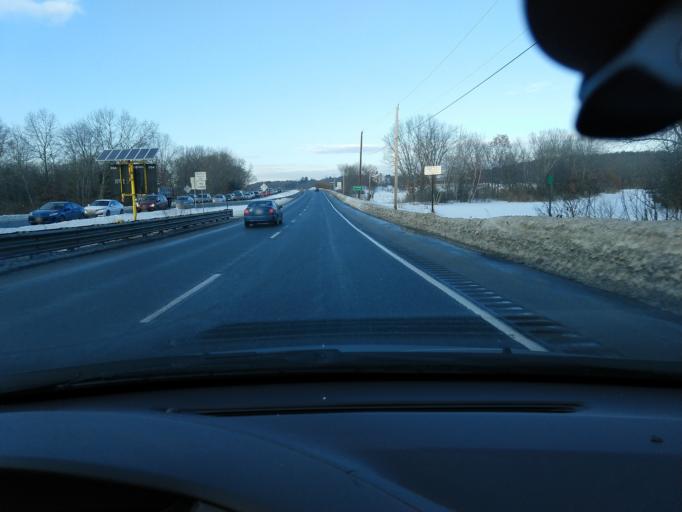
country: US
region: Massachusetts
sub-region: Middlesex County
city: West Concord
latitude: 42.4692
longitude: -71.4069
